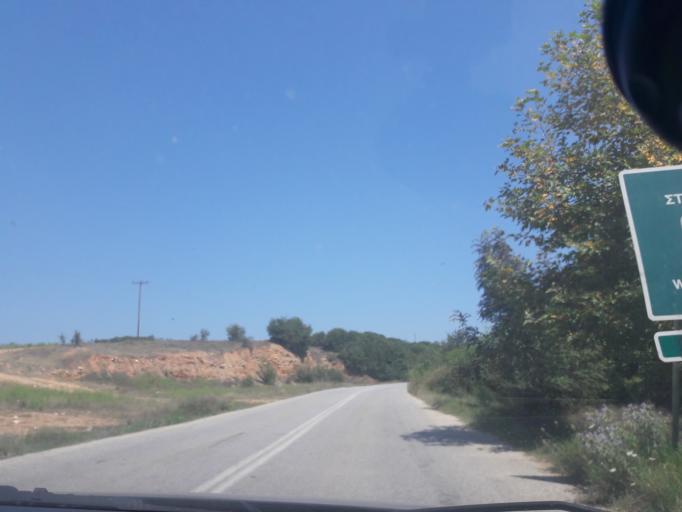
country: GR
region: Central Macedonia
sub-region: Nomos Chalkidikis
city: Megali Panagia
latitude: 40.3705
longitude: 23.6747
